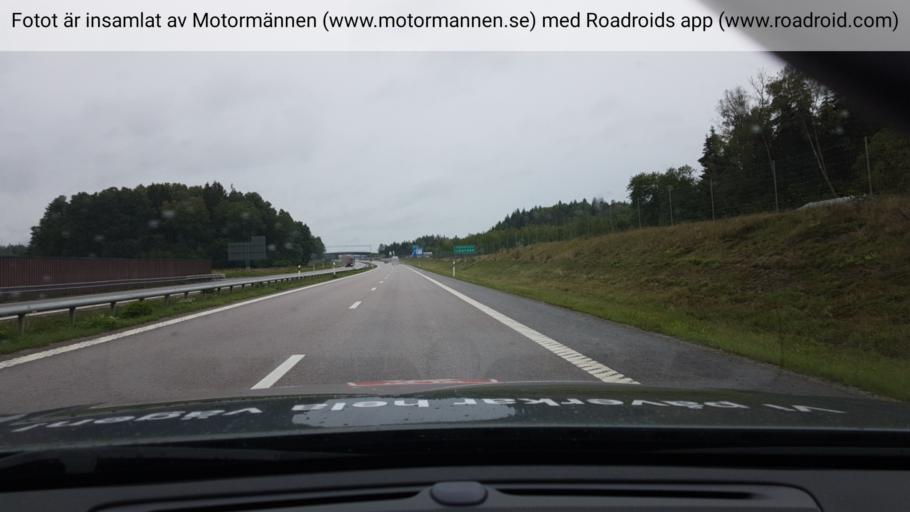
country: SE
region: Stockholm
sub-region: Nynashamns Kommun
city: Osmo
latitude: 58.9704
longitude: 17.9090
